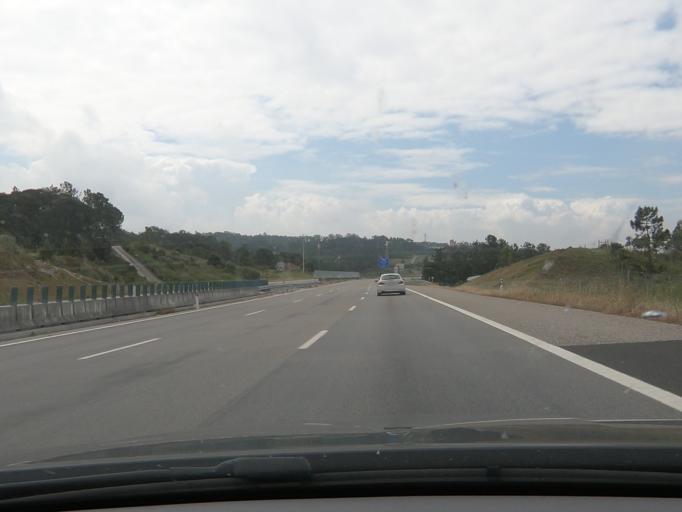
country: PT
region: Leiria
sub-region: Leiria
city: Souto da Carpalhosa
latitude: 39.8366
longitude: -8.8355
